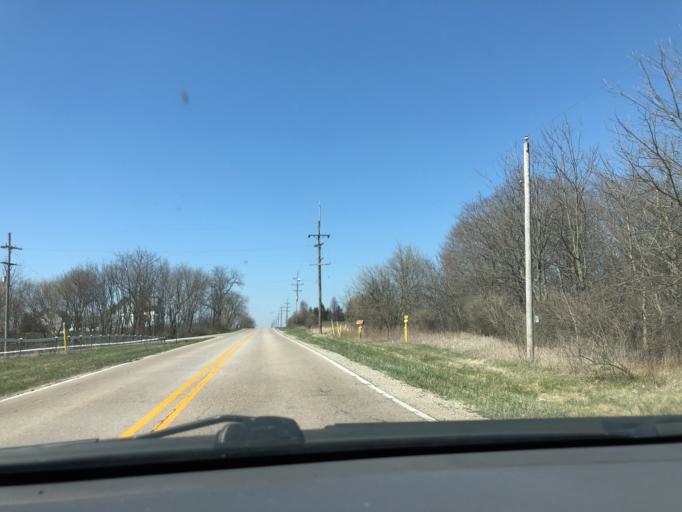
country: US
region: Illinois
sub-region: Kane County
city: Hampshire
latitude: 42.1127
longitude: -88.4912
